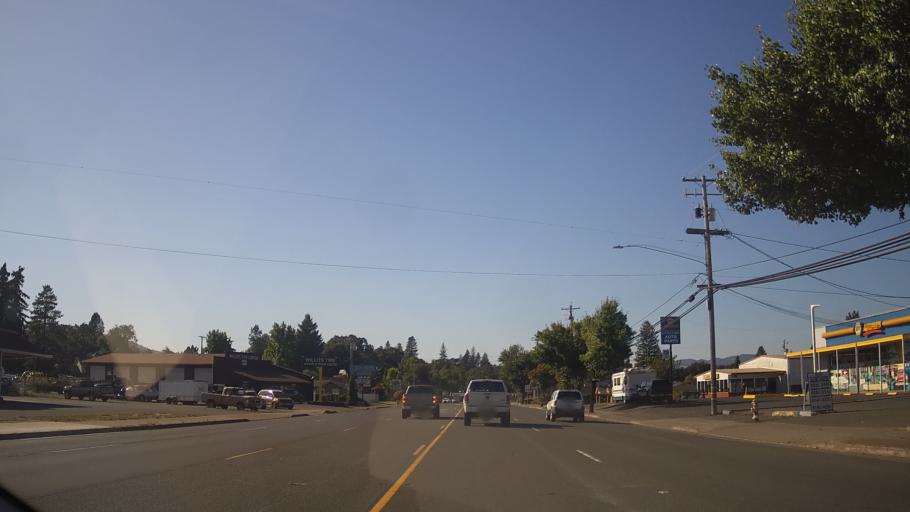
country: US
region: California
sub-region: Mendocino County
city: Willits
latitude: 39.3928
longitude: -123.3479
